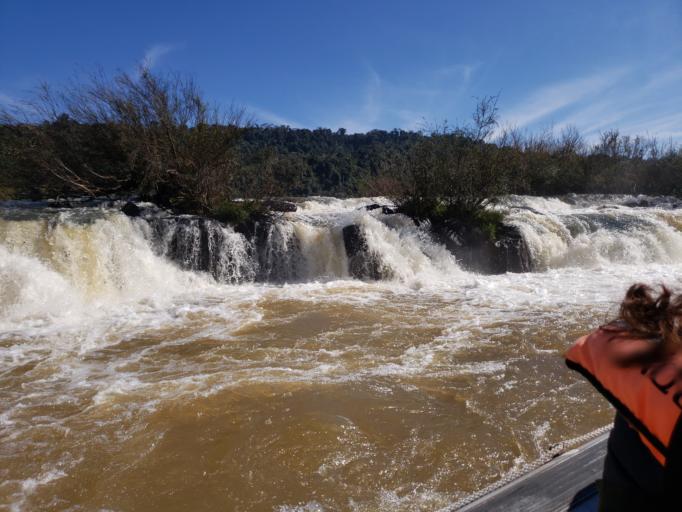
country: BR
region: Rio Grande do Sul
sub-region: Tres Passos
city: Tres Passos
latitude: -27.1483
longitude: -53.8871
